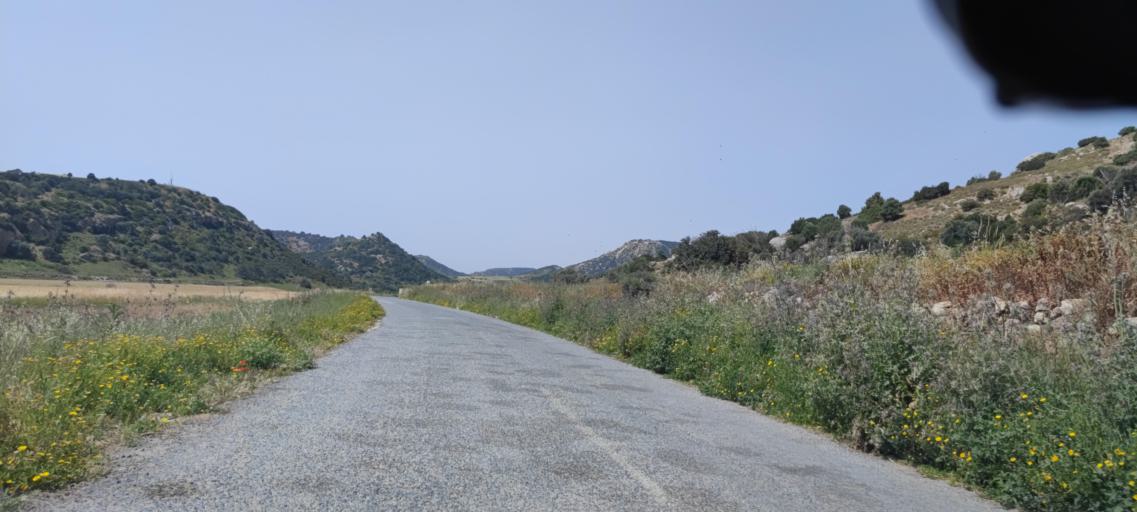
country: CY
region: Ammochostos
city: Rizokarpaso
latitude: 35.5177
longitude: 34.3124
